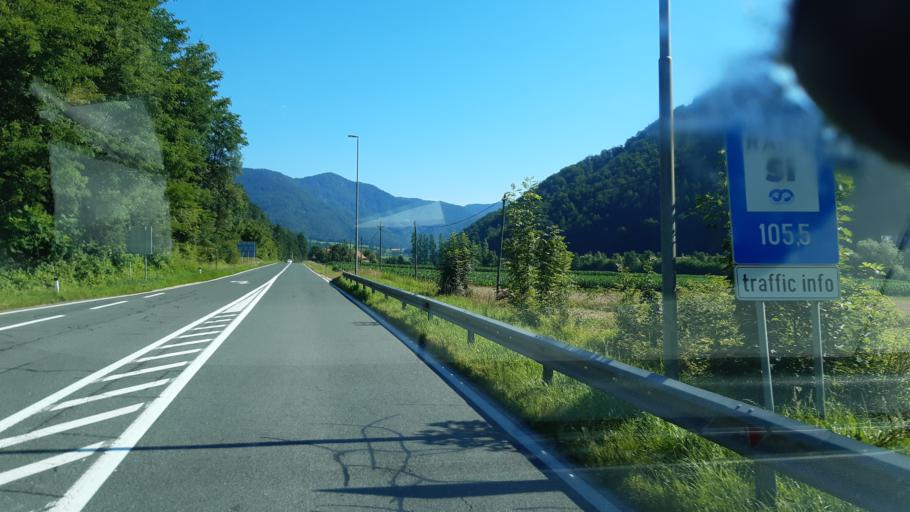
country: SI
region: Vransko
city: Vransko
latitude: 46.2286
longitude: 14.9439
